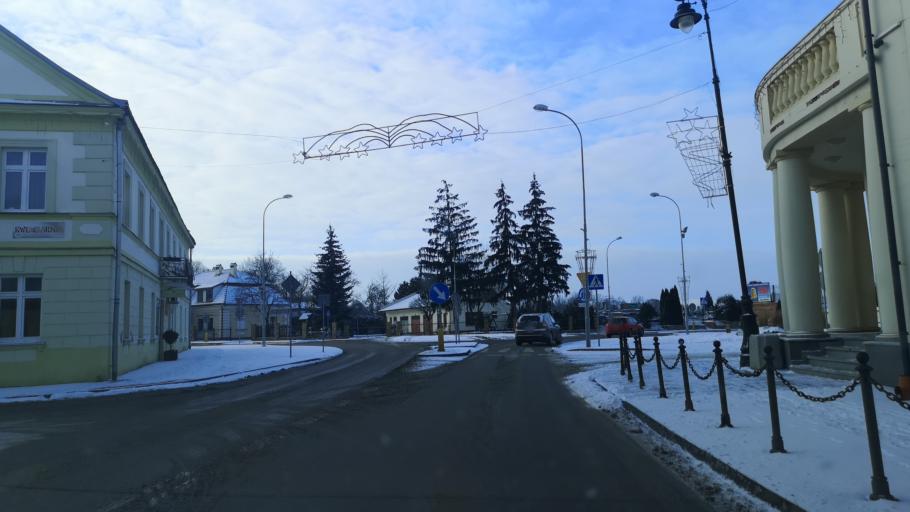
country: PL
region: Subcarpathian Voivodeship
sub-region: Powiat przeworski
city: Sieniawa
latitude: 50.1767
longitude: 22.6089
